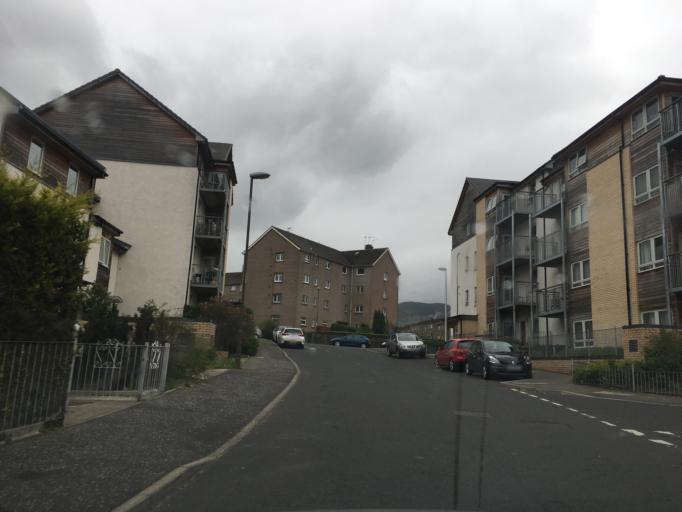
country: GB
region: Scotland
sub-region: Edinburgh
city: Colinton
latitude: 55.9114
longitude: -3.2235
